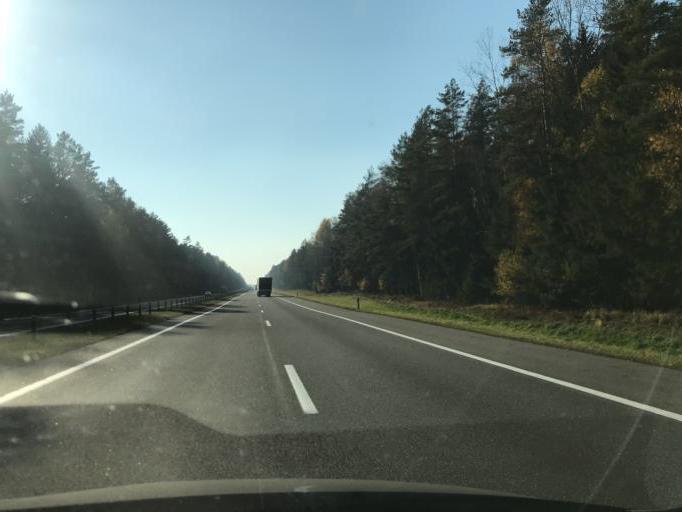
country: BY
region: Minsk
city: Enyerhyetykaw
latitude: 53.5670
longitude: 26.9937
